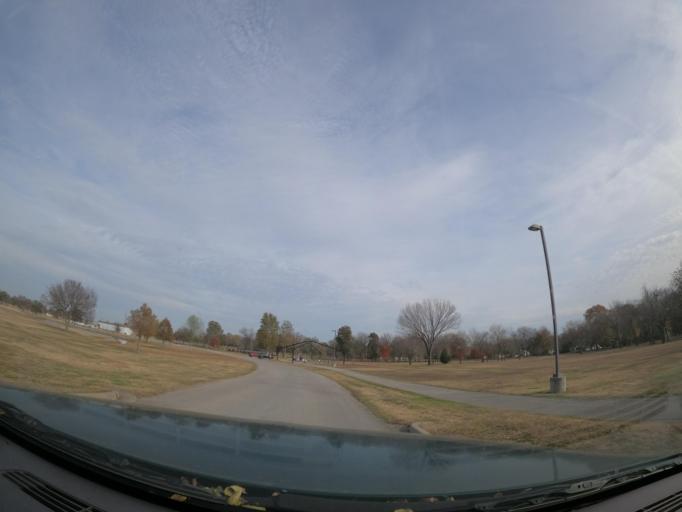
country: US
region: Oklahoma
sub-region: Tulsa County
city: Turley
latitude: 36.2435
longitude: -95.9573
